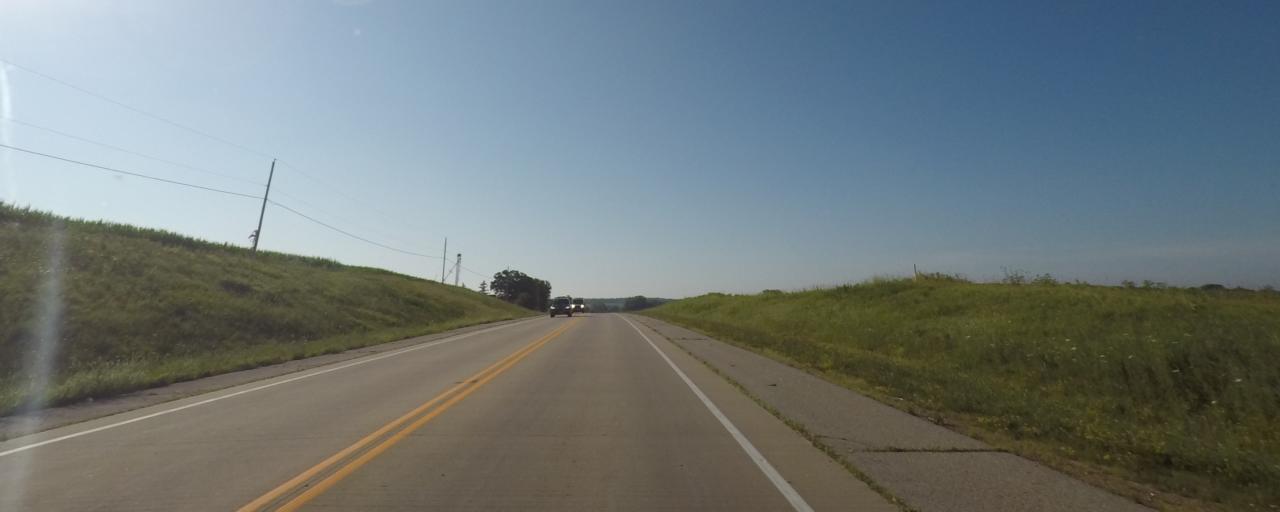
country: US
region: Wisconsin
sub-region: Jefferson County
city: Lake Ripley
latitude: 42.9838
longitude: -88.9697
